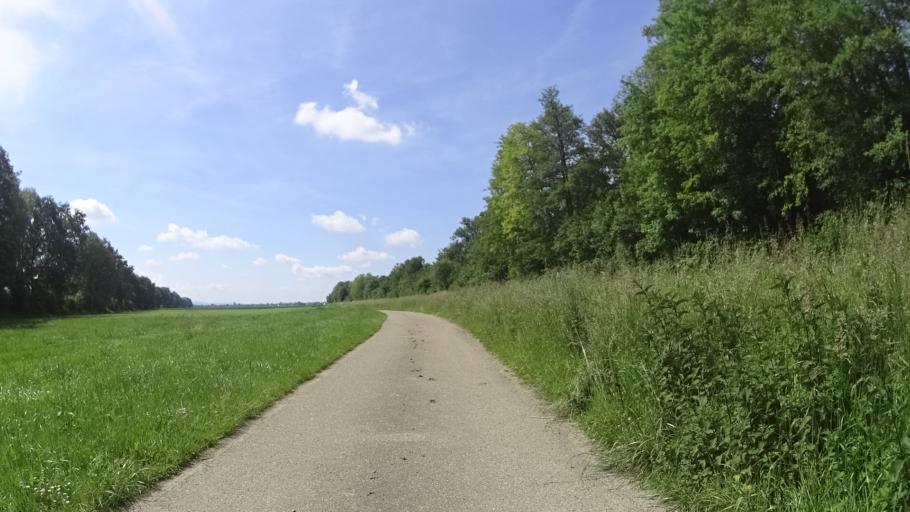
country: DE
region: Baden-Wuerttemberg
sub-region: Freiburg Region
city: Schutterwald
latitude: 48.4886
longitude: 7.8181
